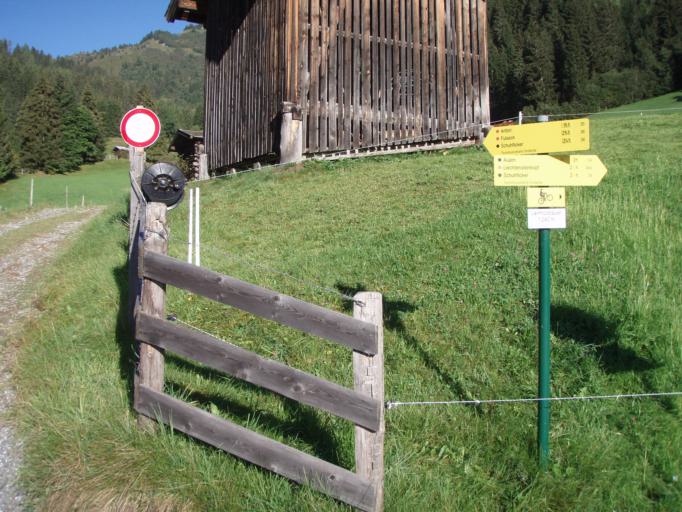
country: AT
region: Salzburg
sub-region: Politischer Bezirk Sankt Johann im Pongau
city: Dorfgastein
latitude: 47.2483
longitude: 13.1787
